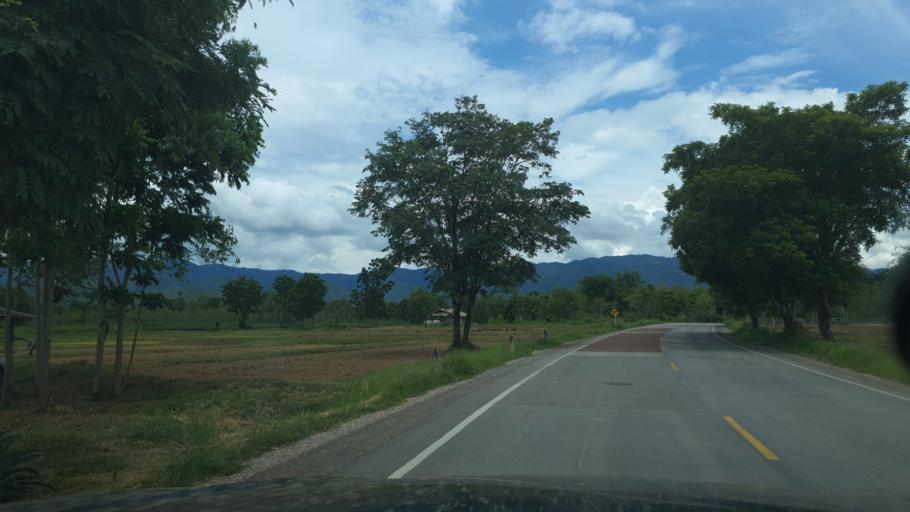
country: TH
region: Lampang
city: Sop Prap
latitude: 17.9194
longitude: 99.3867
